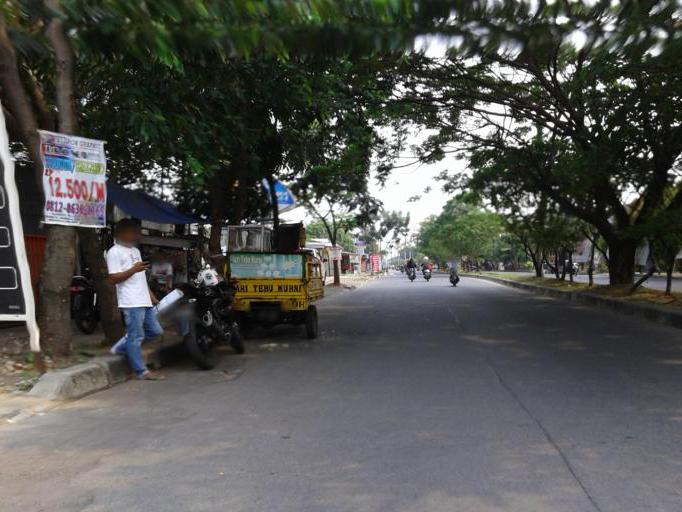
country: ID
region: West Java
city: Pamulang
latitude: -6.3489
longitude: 106.7763
